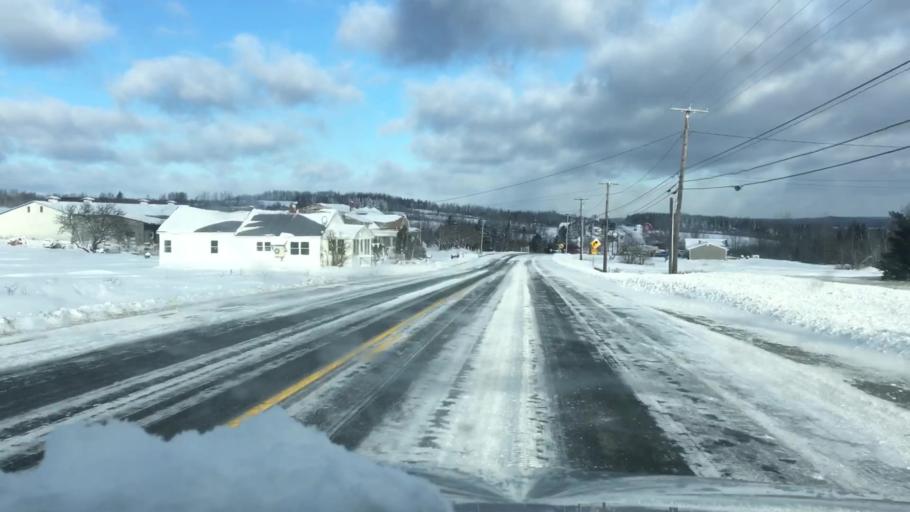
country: US
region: Maine
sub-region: Aroostook County
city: Caribou
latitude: 46.9529
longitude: -68.0260
